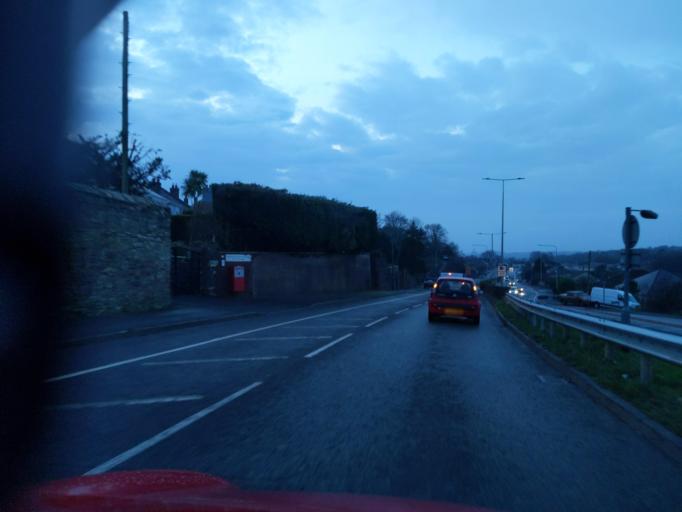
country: GB
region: England
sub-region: Plymouth
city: Plymstock
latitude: 50.3625
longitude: -4.0701
